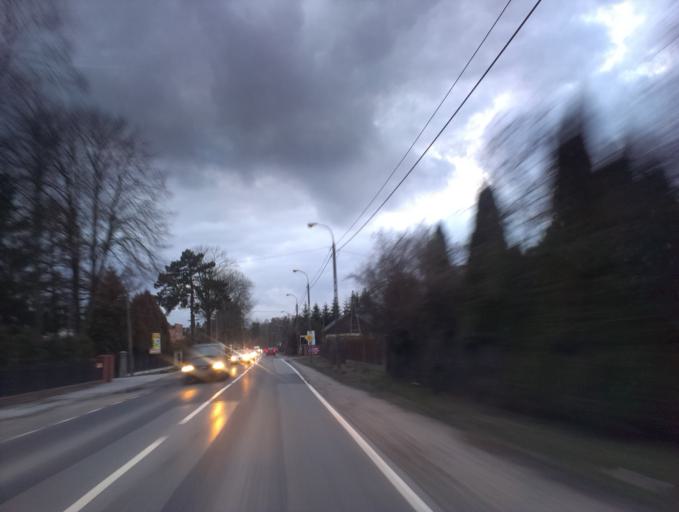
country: PL
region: Masovian Voivodeship
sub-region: Powiat piaseczynski
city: Jozefoslaw
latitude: 52.0839
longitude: 21.0592
